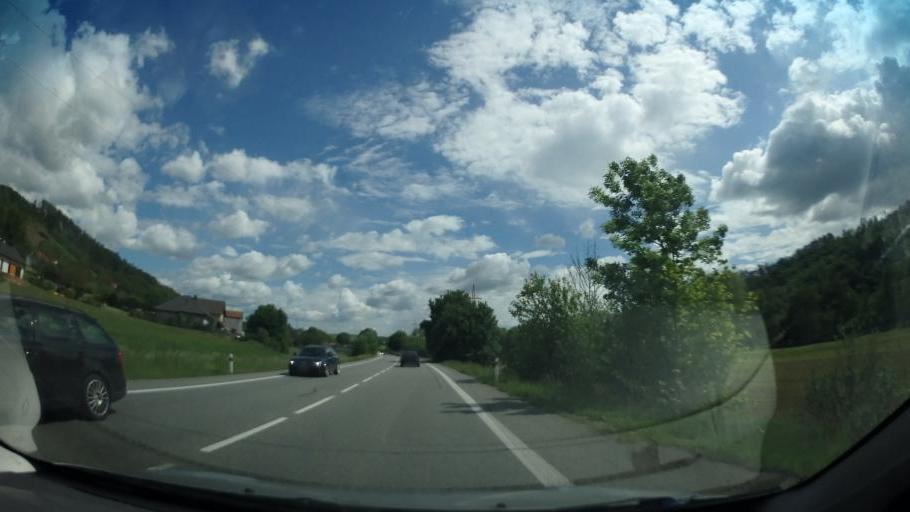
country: CZ
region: South Moravian
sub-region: Okres Blansko
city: Letovice
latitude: 49.5270
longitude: 16.5826
